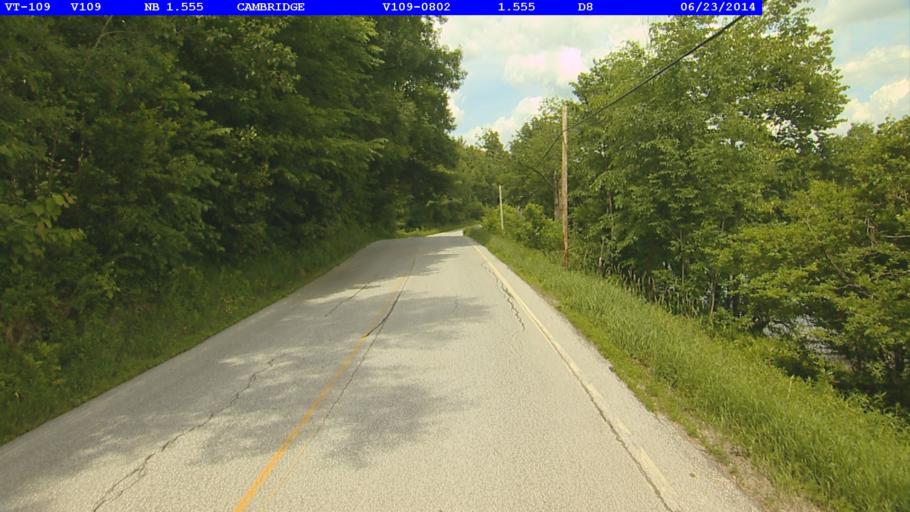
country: US
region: Vermont
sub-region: Lamoille County
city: Johnson
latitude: 44.6626
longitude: -72.8046
